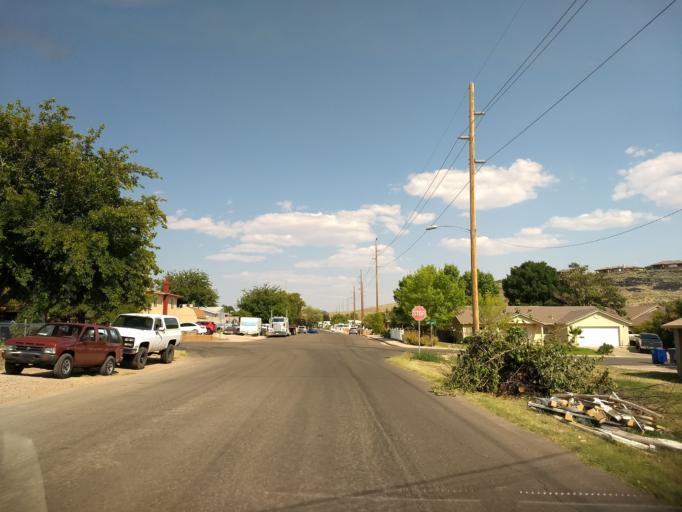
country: US
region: Utah
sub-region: Washington County
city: Washington
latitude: 37.1277
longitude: -113.5070
